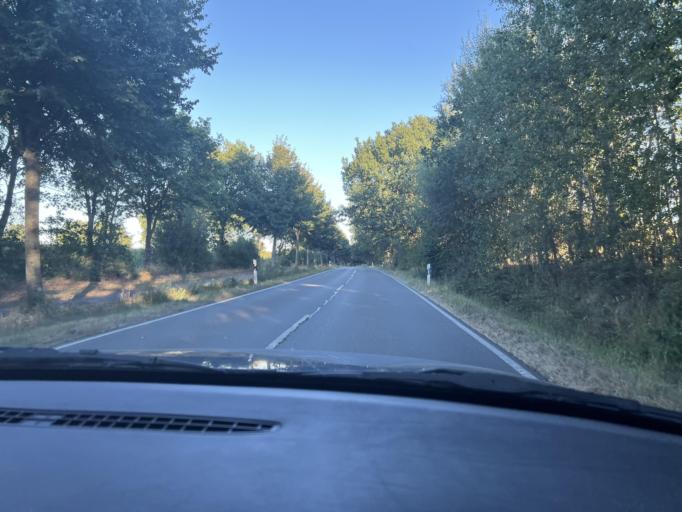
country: DE
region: Schleswig-Holstein
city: Kleve
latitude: 54.2919
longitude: 9.1363
